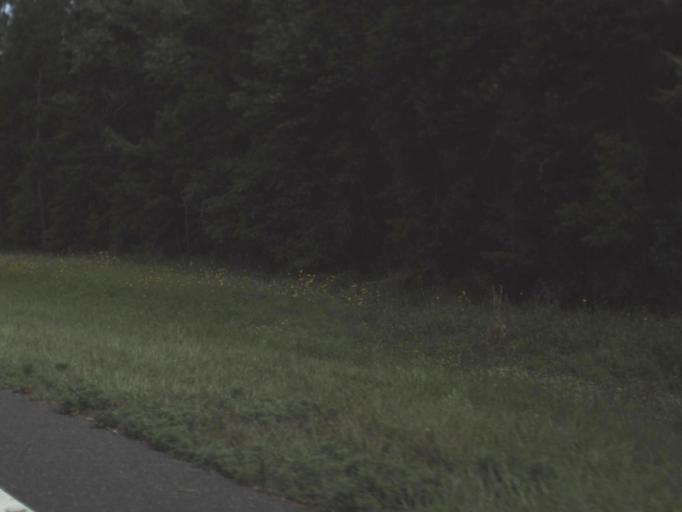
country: US
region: Florida
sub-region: Taylor County
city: Perry
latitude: 30.0305
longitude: -83.5412
